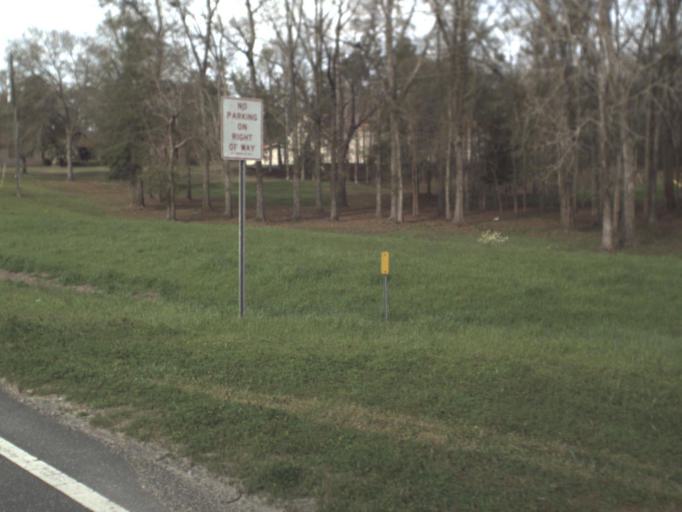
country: US
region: Florida
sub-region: Jefferson County
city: Monticello
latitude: 30.5620
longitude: -83.8701
